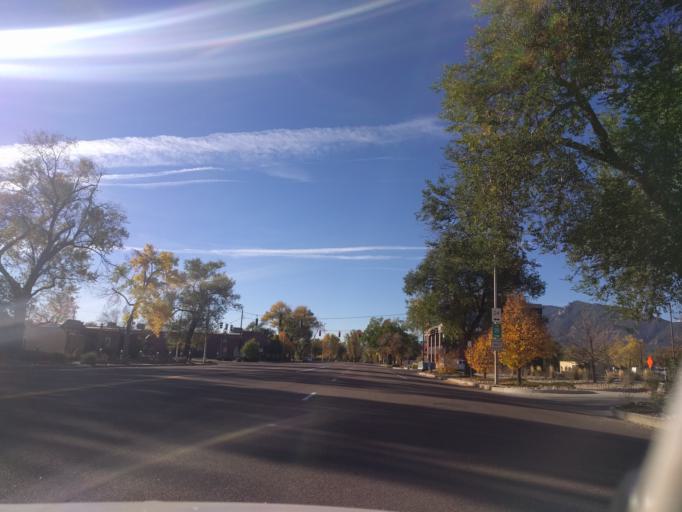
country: US
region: Colorado
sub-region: El Paso County
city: Colorado Springs
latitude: 38.8277
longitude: -104.8258
